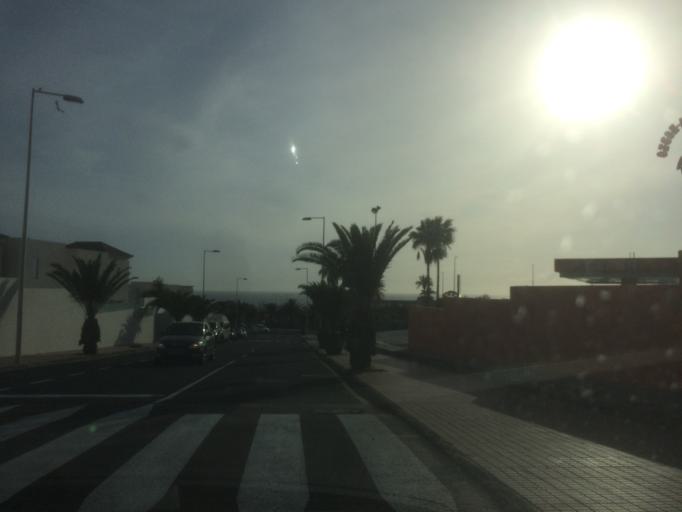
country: ES
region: Canary Islands
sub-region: Provincia de Santa Cruz de Tenerife
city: Playa de las Americas
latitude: 28.0901
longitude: -16.7276
